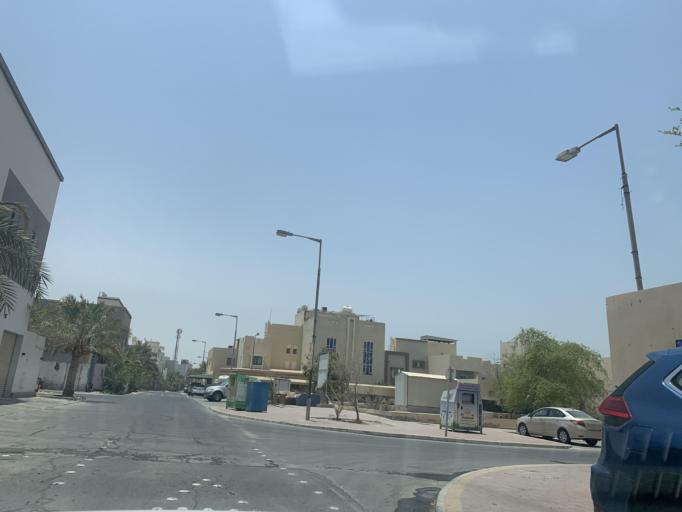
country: BH
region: Manama
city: Jidd Hafs
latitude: 26.2103
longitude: 50.4718
